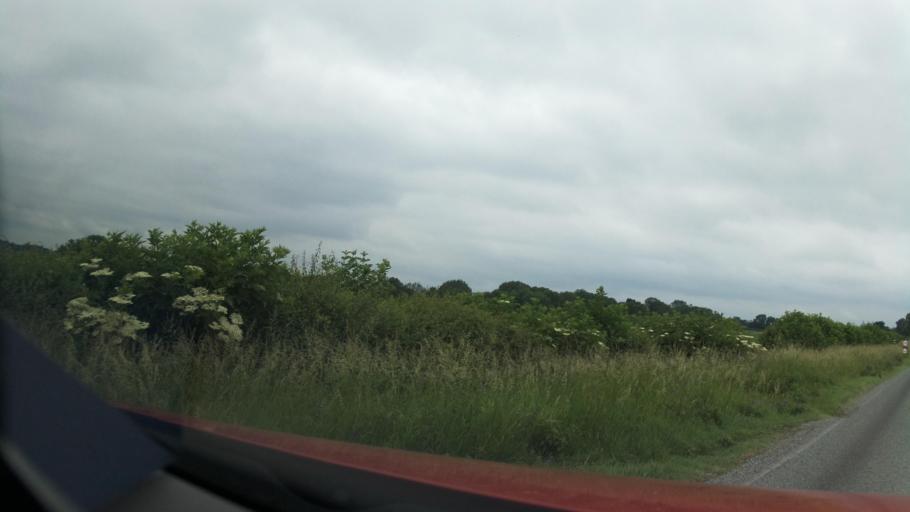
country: GB
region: England
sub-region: District of Rutland
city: Exton
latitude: 52.6718
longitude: -0.6478
